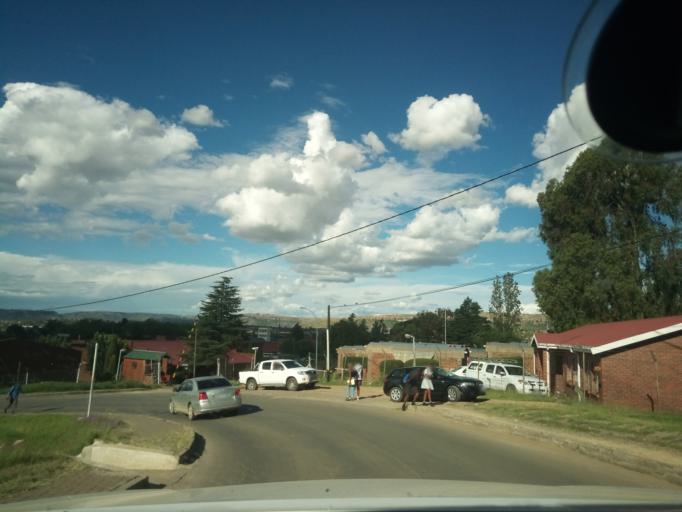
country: LS
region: Maseru
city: Maseru
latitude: -29.3270
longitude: 27.5007
